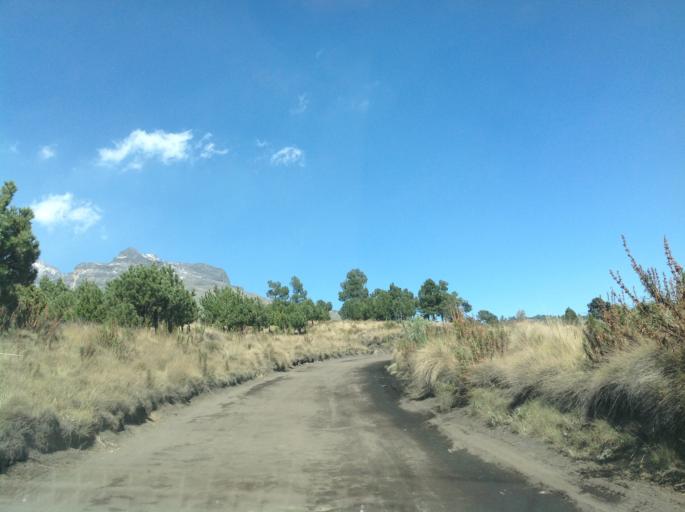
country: MX
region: Mexico
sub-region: Amecameca
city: San Diego Huehuecalco
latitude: 19.1121
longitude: -98.6433
